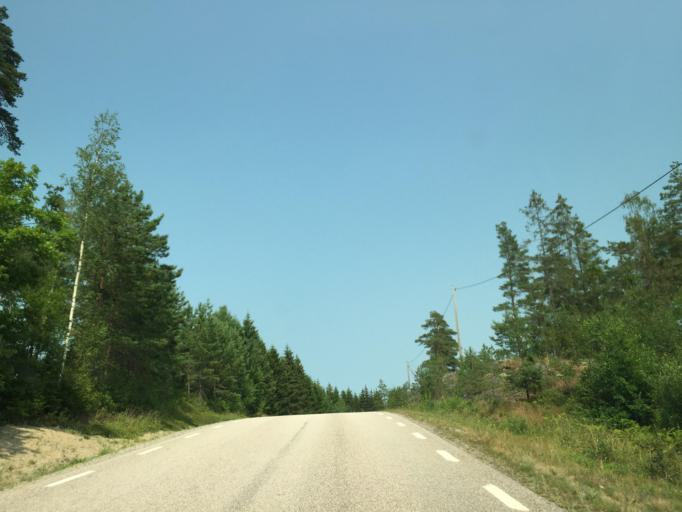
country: SE
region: Vaestra Goetaland
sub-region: Lilla Edets Kommun
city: Lilla Edet
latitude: 58.1567
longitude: 12.0652
